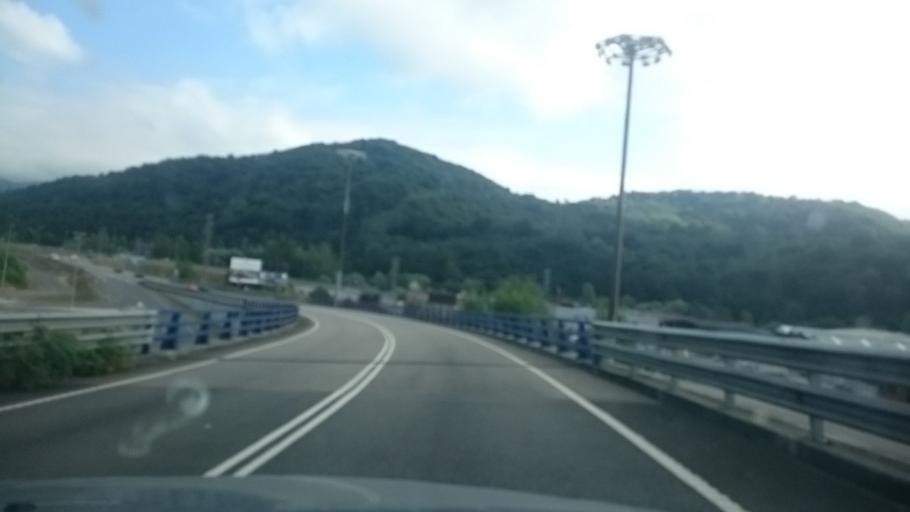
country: ES
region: Asturias
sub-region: Province of Asturias
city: Sama
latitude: 43.3248
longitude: -5.7181
